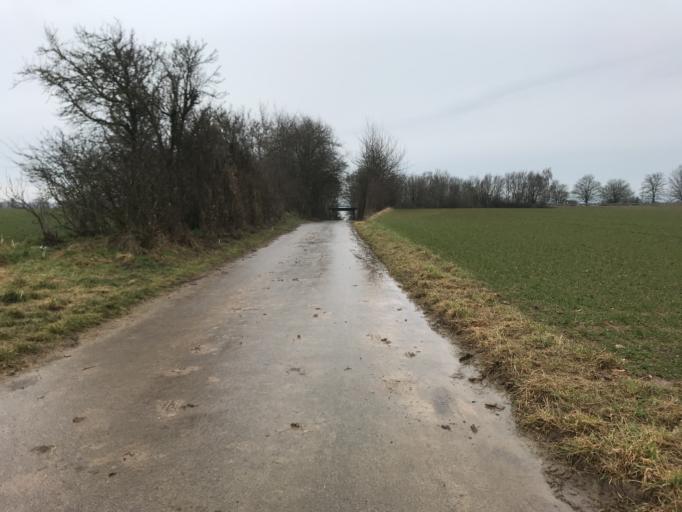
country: DE
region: Rheinland-Pfalz
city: Essenheim
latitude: 49.9371
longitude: 8.1589
